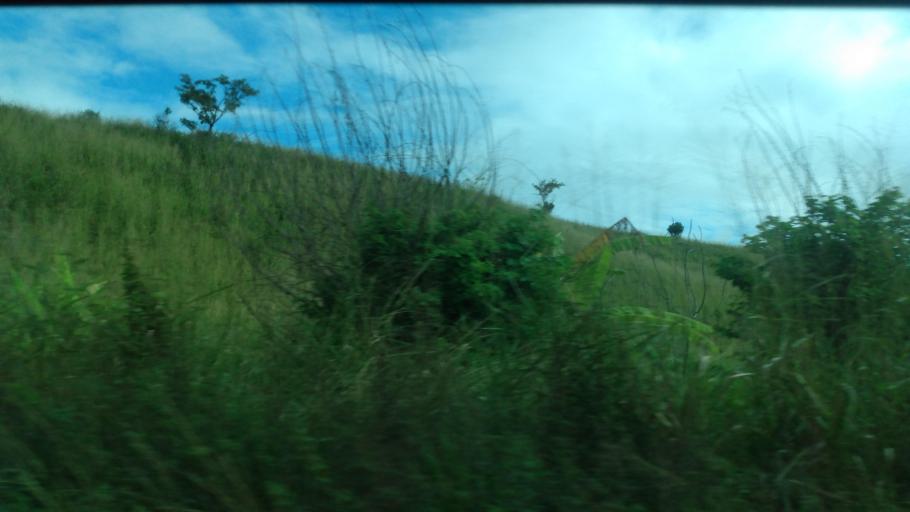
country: BR
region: Pernambuco
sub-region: Catende
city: Catende
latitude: -8.6900
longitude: -35.7033
